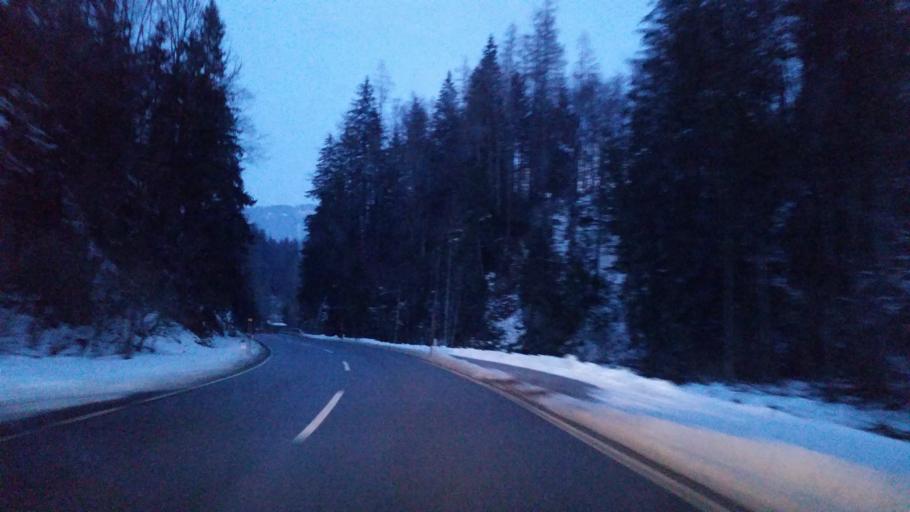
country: AT
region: Salzburg
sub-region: Politischer Bezirk Hallein
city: Abtenau
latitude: 47.5030
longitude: 13.4238
